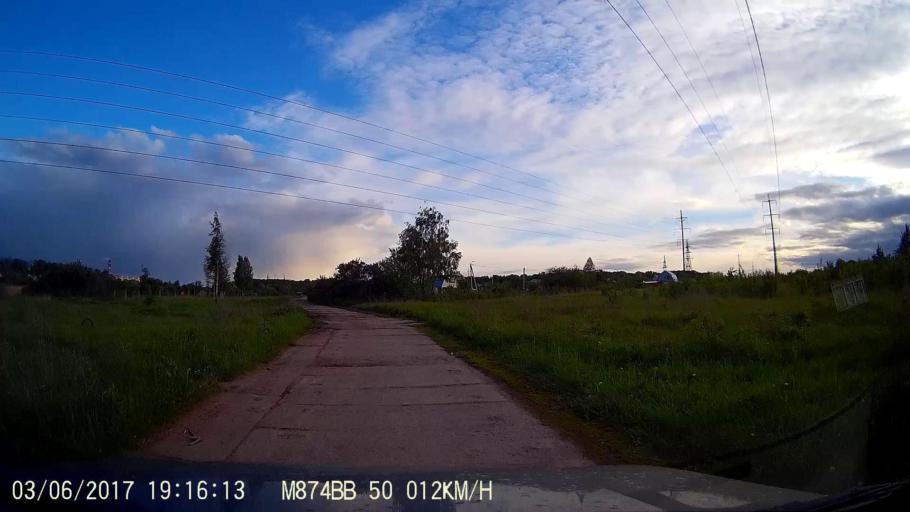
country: RU
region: Moskovskaya
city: Sychevo
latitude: 55.0722
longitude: 38.7388
